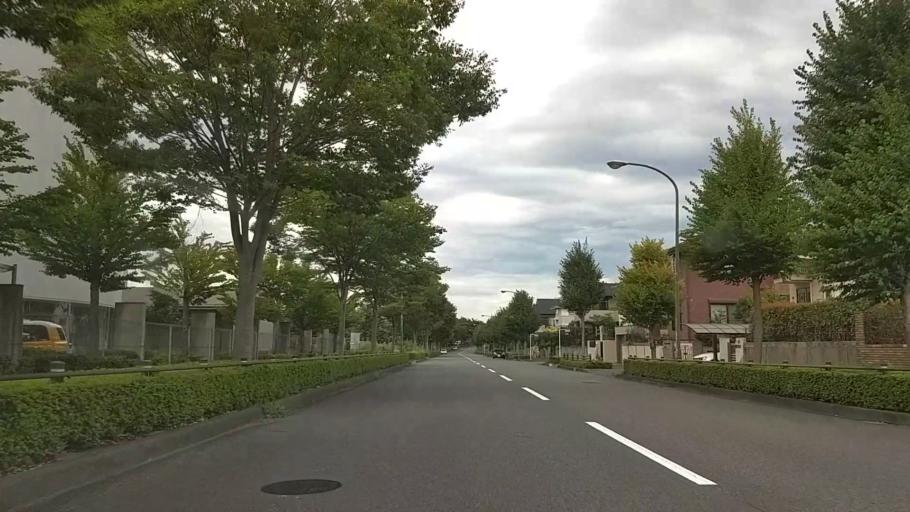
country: JP
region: Tokyo
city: Hachioji
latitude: 35.6267
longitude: 139.3170
